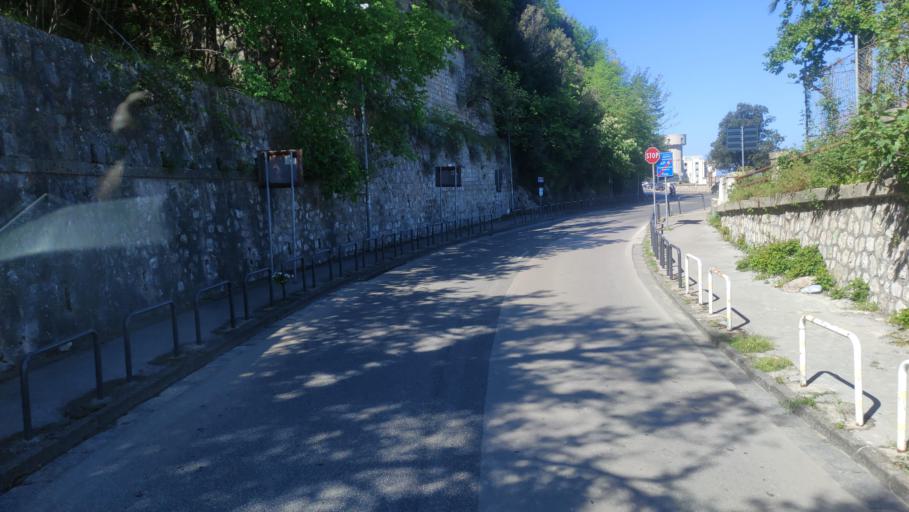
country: IT
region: Campania
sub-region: Provincia di Napoli
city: Vico Equense
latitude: 40.6882
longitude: 14.4559
